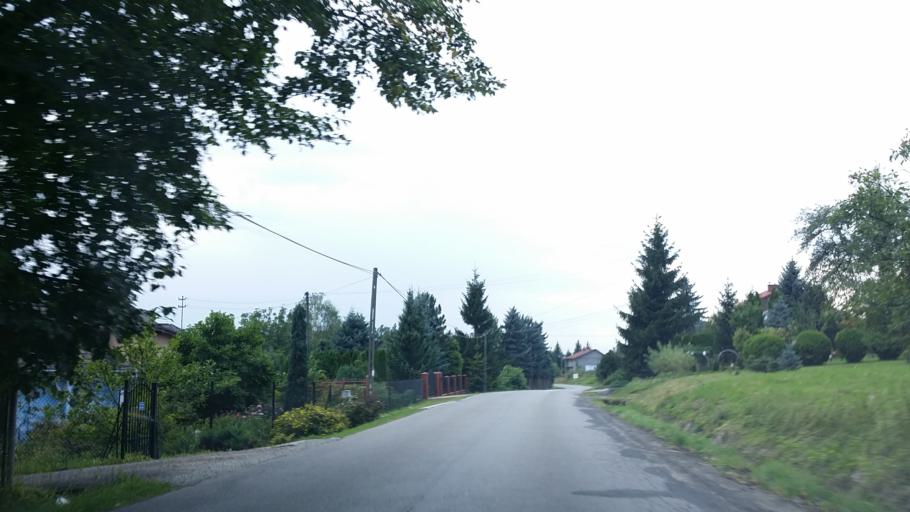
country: PL
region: Lesser Poland Voivodeship
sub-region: Powiat wielicki
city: Pawlikowice
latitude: 49.9747
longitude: 20.0210
